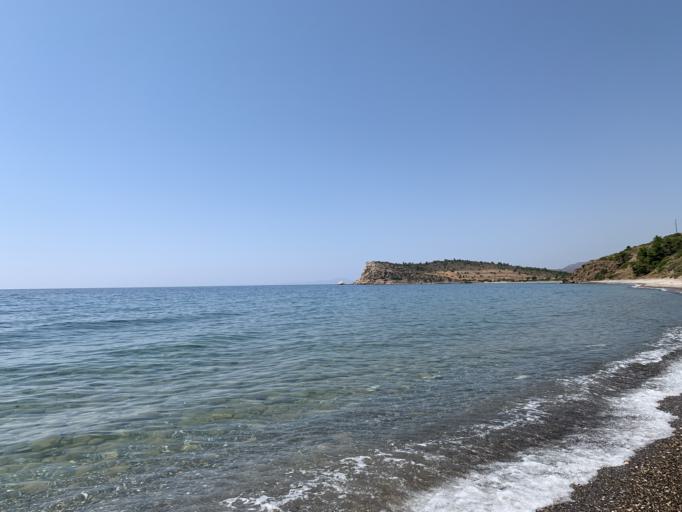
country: GR
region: North Aegean
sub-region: Chios
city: Vrontados
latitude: 38.4422
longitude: 25.9568
